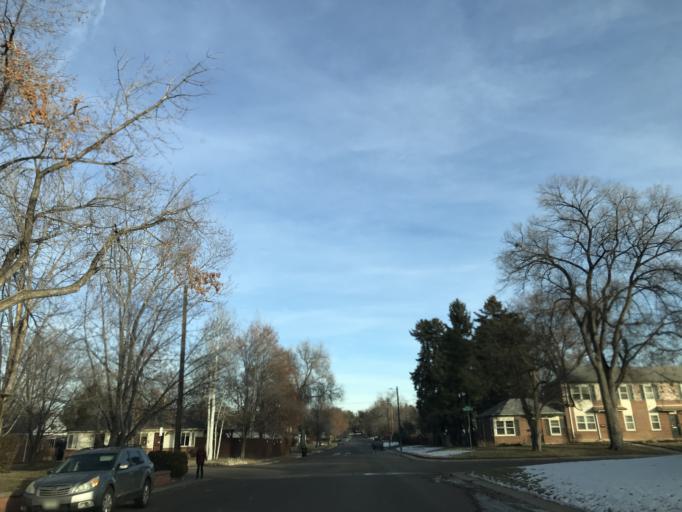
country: US
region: Colorado
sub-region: Arapahoe County
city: Glendale
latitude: 39.7351
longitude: -104.9178
